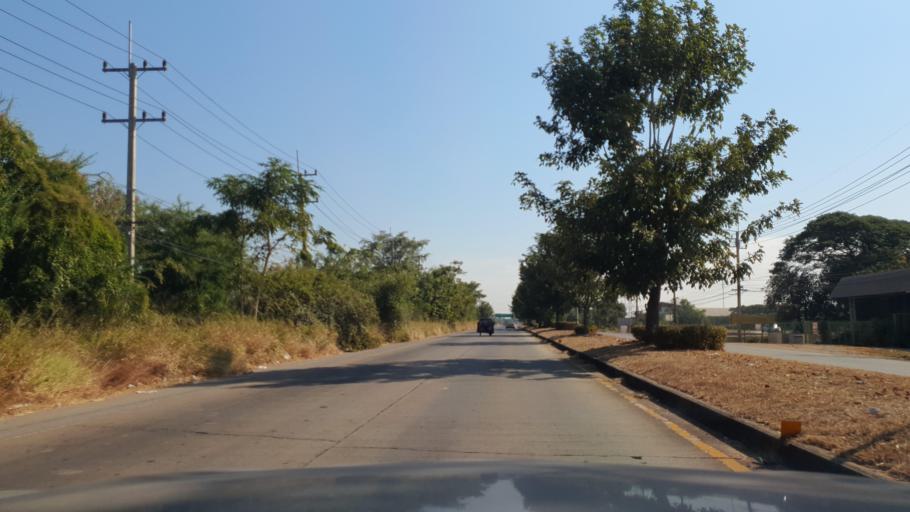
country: TH
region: Khon Kaen
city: Khon Kaen
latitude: 16.4376
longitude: 102.9077
